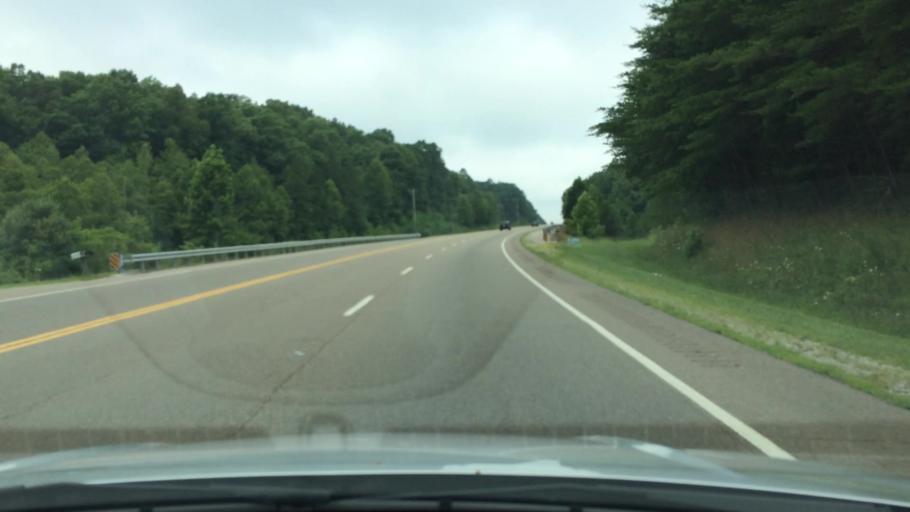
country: US
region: Tennessee
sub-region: Scott County
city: Huntsville
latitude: 36.3871
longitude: -84.4254
